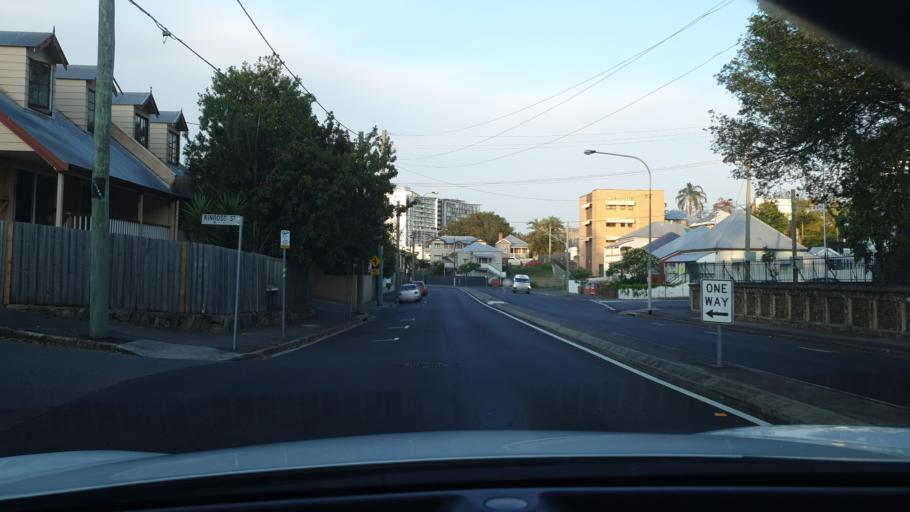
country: AU
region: Queensland
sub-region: Brisbane
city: Fortitude Valley
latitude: -27.4568
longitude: 153.0278
